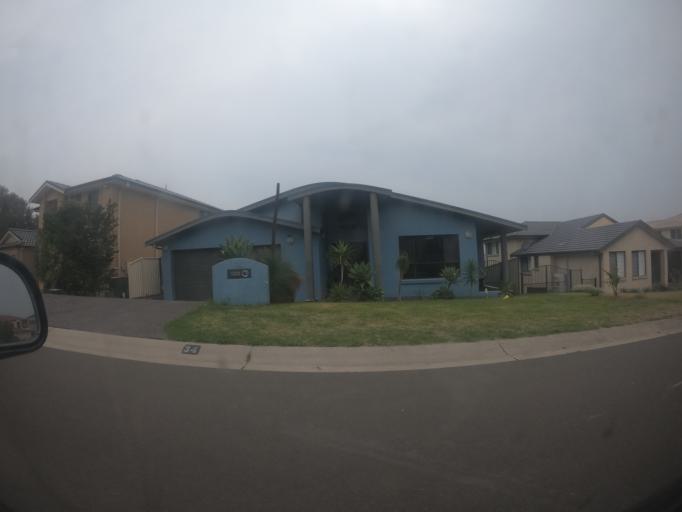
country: AU
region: New South Wales
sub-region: Shellharbour
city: Flinders
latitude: -34.5925
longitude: 150.8520
